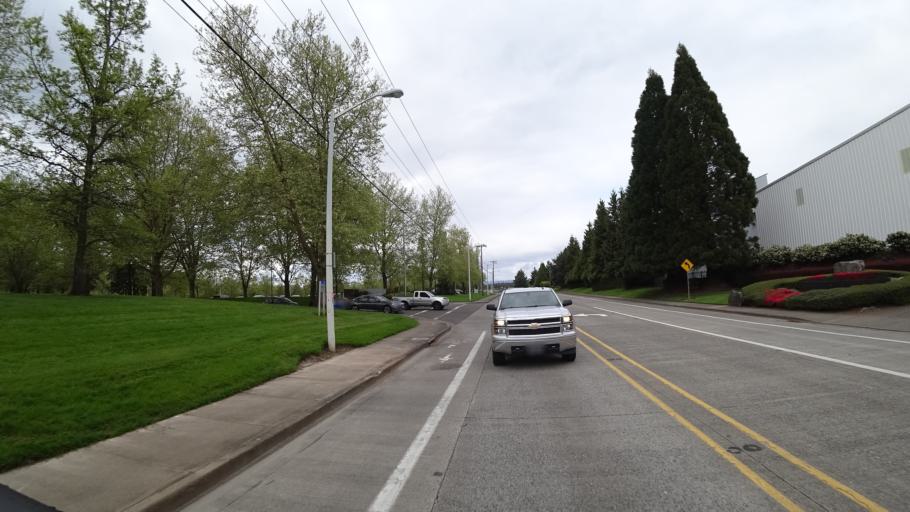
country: US
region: Oregon
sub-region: Washington County
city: Hillsboro
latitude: 45.5419
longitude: -122.9572
